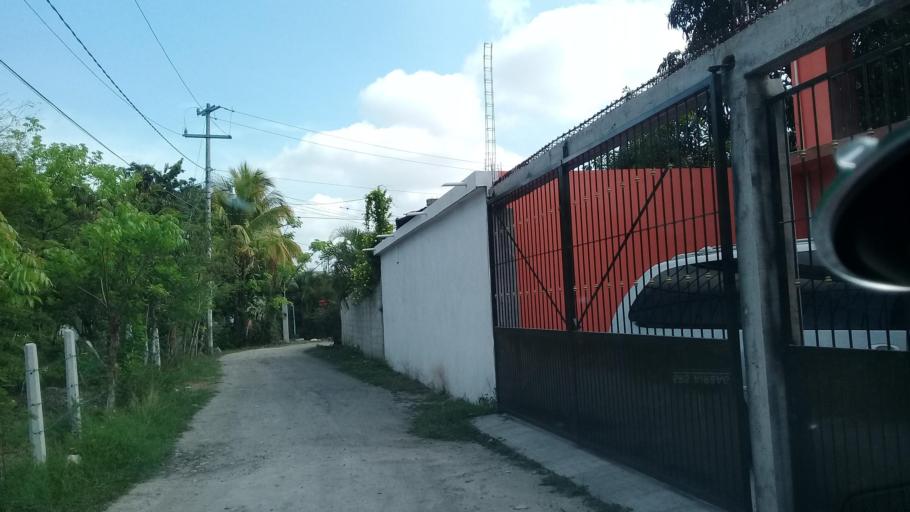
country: MX
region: Veracruz
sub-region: Emiliano Zapata
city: Plan del Rio
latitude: 19.3888
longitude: -96.6381
